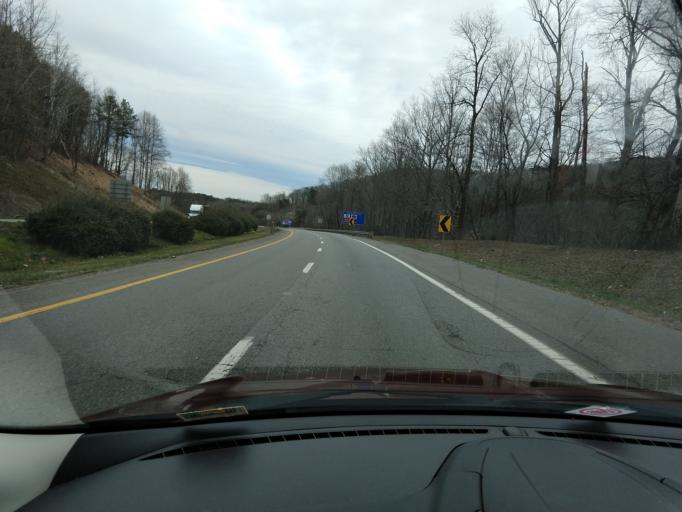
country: US
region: Virginia
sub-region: Henry County
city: Collinsville
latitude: 36.7245
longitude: -79.9411
